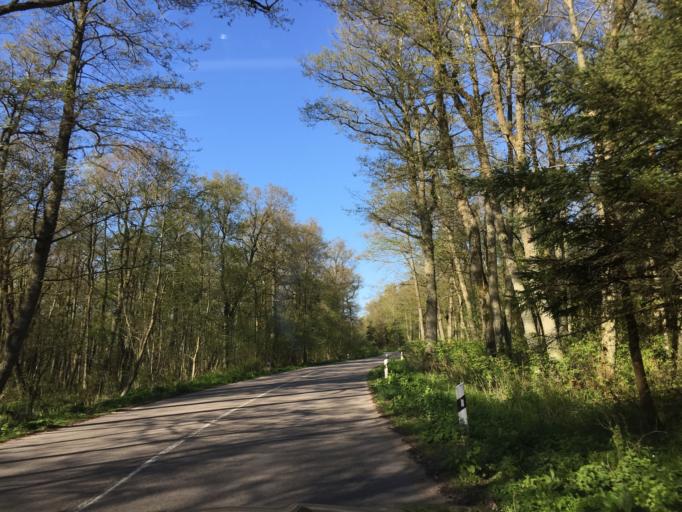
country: LT
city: Nida
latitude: 55.1945
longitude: 20.8630
